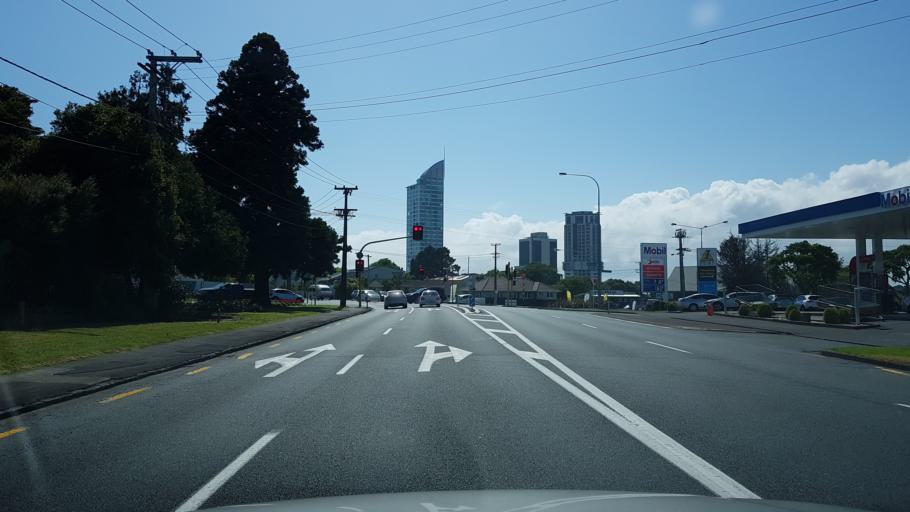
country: NZ
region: Auckland
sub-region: Auckland
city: North Shore
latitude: -36.7900
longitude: 174.7642
